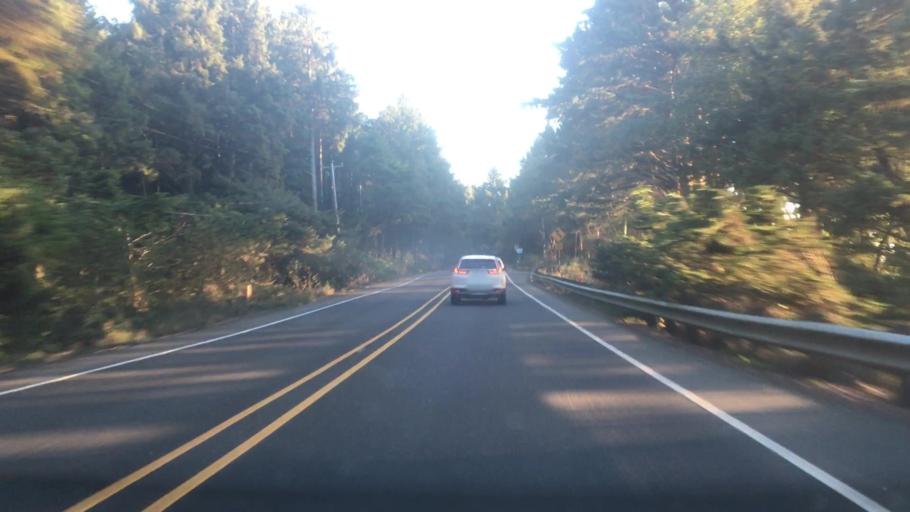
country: US
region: Oregon
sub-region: Clatsop County
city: Cannon Beach
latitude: 45.8443
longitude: -123.9593
